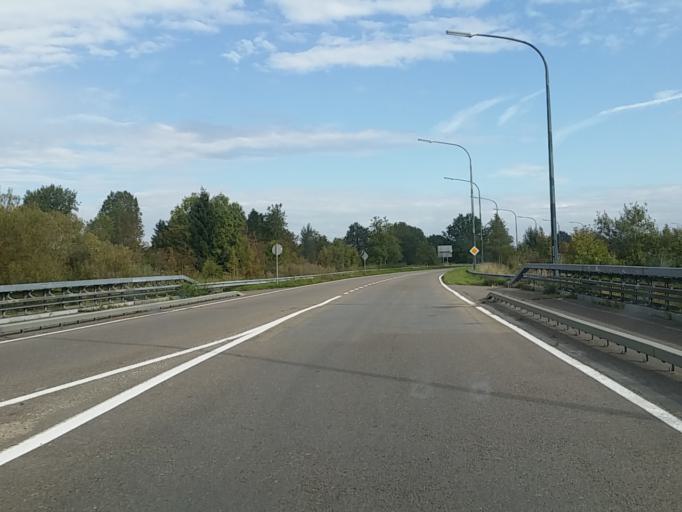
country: BE
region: Wallonia
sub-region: Province du Luxembourg
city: Etalle
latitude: 49.6733
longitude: 5.5904
